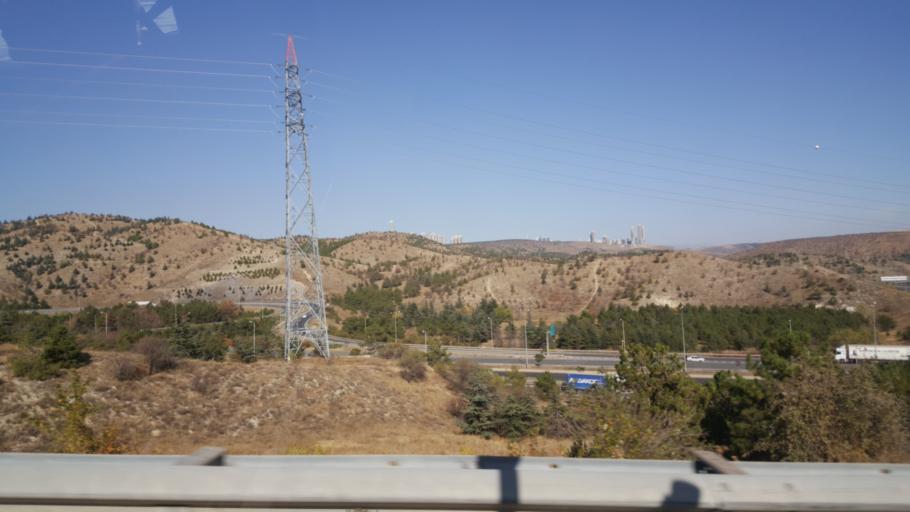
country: TR
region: Ankara
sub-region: Goelbasi
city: Golbasi
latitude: 39.8111
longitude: 32.8000
